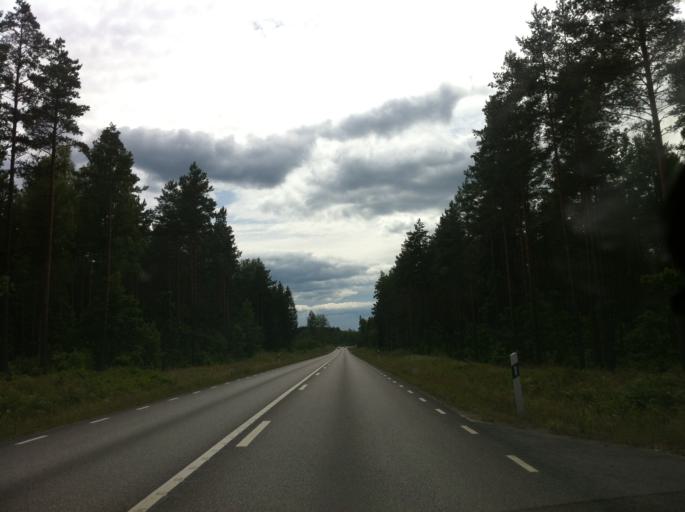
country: SE
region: Kronoberg
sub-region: Tingsryds Kommun
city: Tingsryd
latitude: 56.5194
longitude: 15.1635
